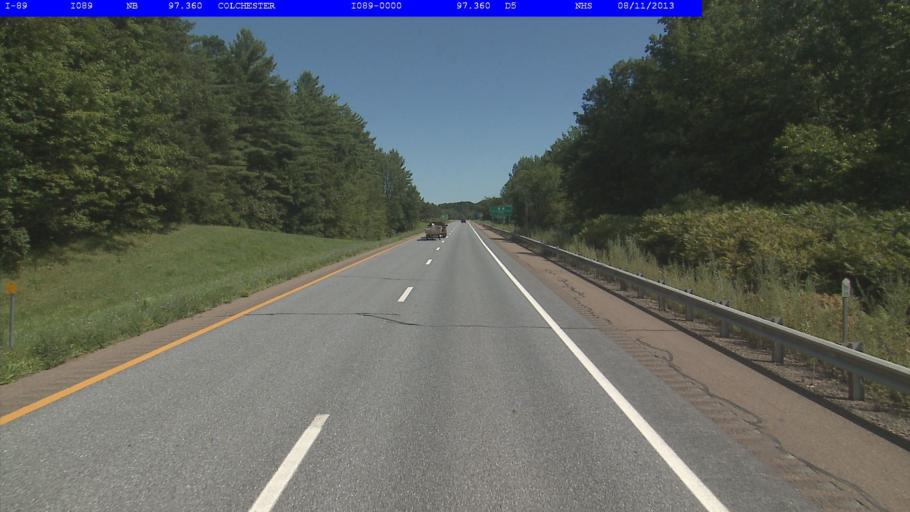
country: US
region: Vermont
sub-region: Chittenden County
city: Colchester
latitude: 44.5829
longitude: -73.1742
